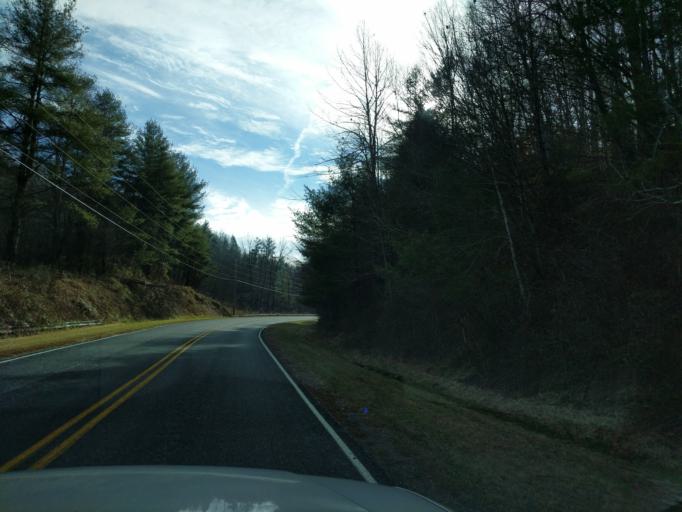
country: US
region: North Carolina
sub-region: Haywood County
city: Cove Creek
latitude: 35.6631
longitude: -82.9958
